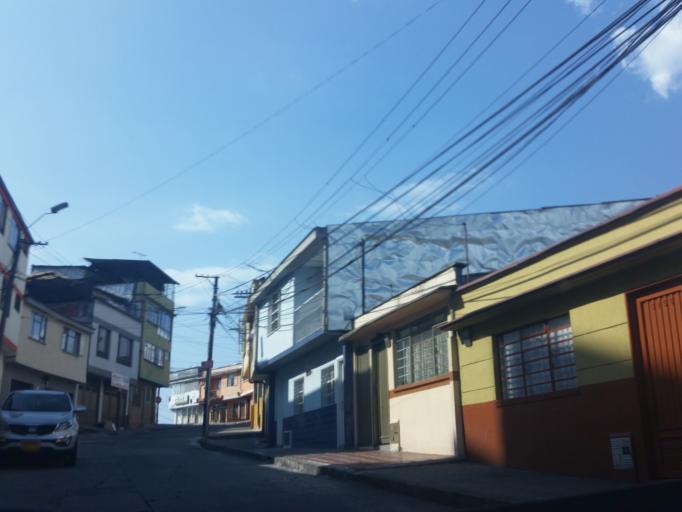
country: CO
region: Caldas
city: Manizales
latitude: 5.0673
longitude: -75.4955
